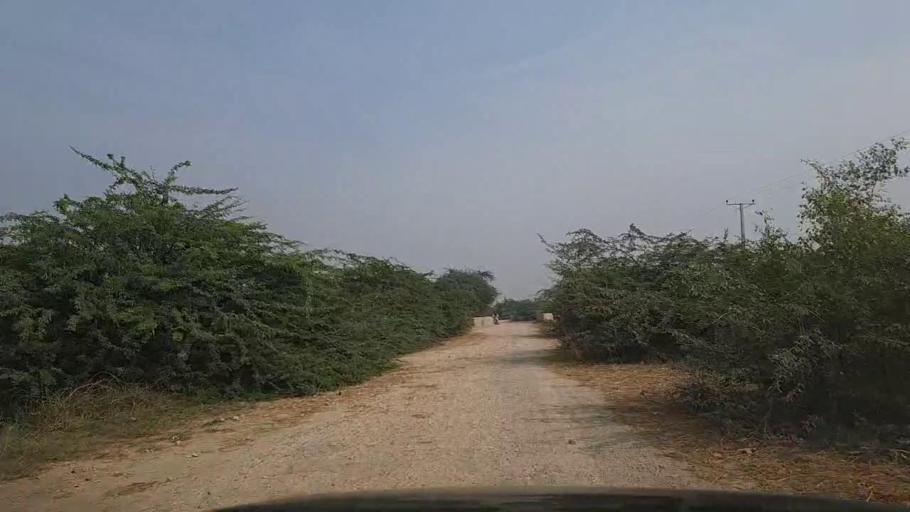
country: PK
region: Sindh
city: Mirpur Sakro
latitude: 24.4023
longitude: 67.7470
